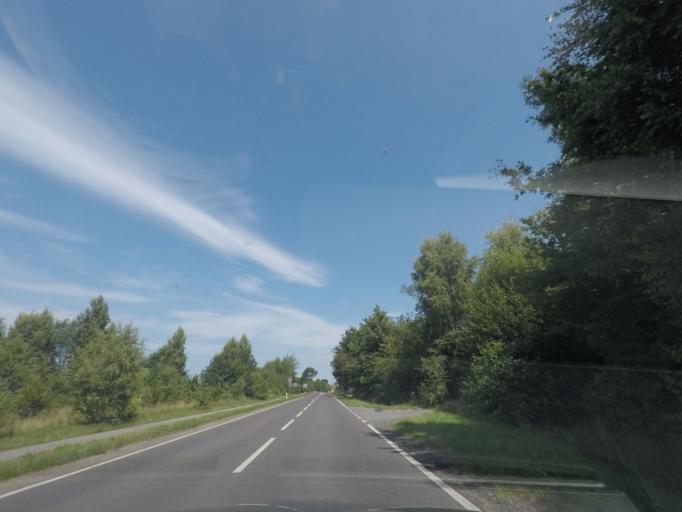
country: PL
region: West Pomeranian Voivodeship
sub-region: Powiat koszalinski
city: Sianow
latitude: 54.3276
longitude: 16.3109
